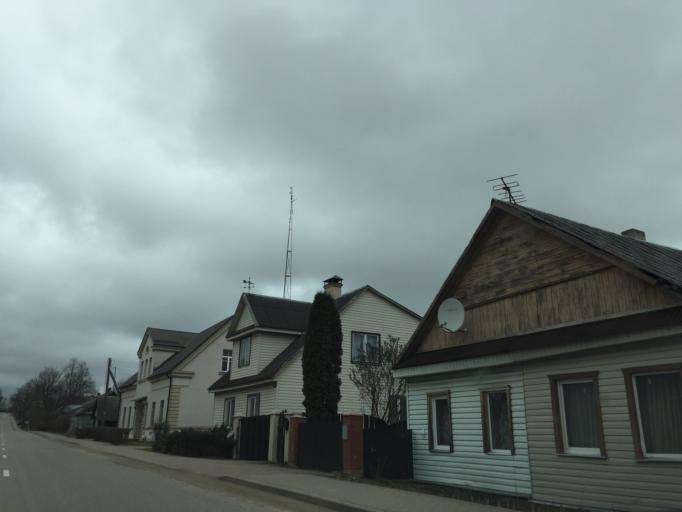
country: LV
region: Ilukste
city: Ilukste
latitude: 55.9789
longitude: 26.2953
